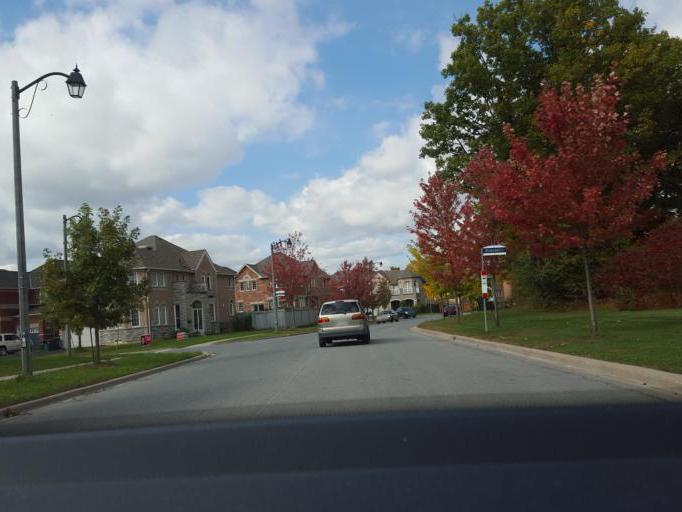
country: CA
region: Ontario
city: Markham
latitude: 43.8333
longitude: -79.2250
